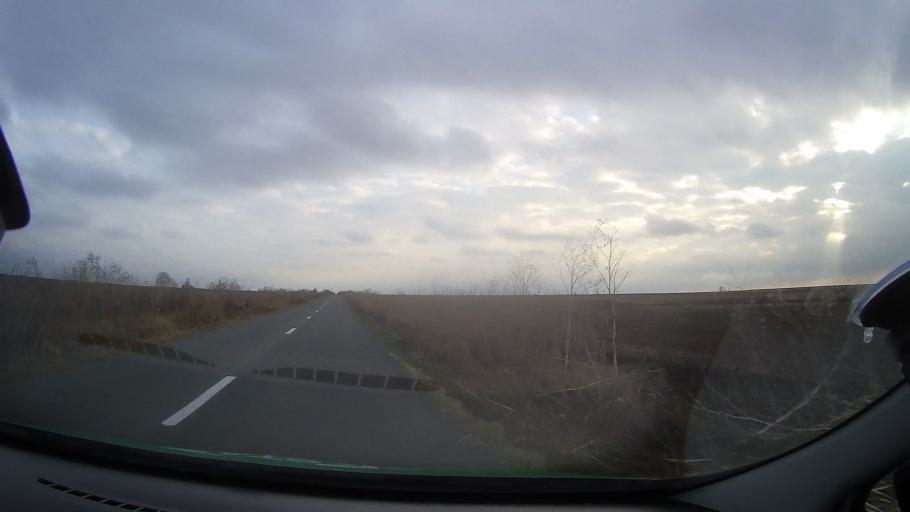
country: RO
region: Constanta
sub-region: Comuna Pestera
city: Pestera
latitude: 44.1454
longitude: 28.1156
